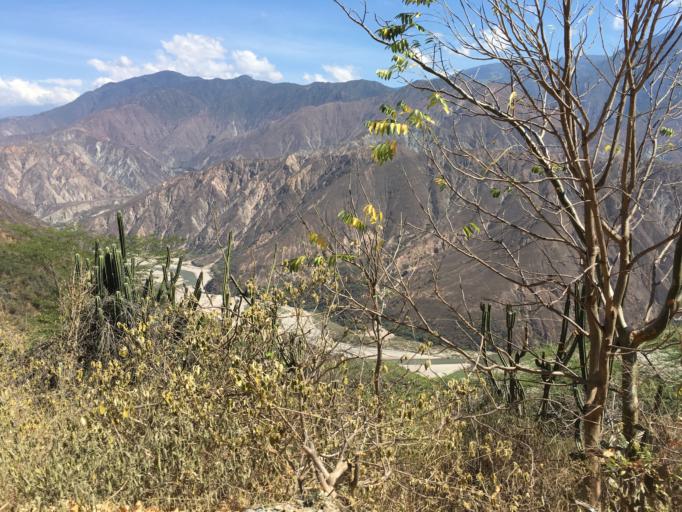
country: CO
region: Santander
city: Aratoca
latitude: 6.7735
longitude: -72.9941
